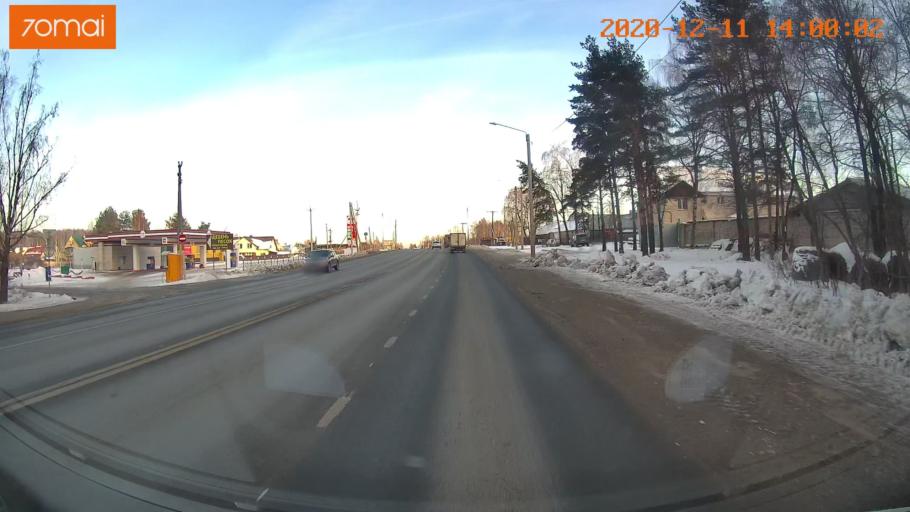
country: RU
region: Kostroma
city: Oktyabr'skiy
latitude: 57.7837
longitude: 41.0219
